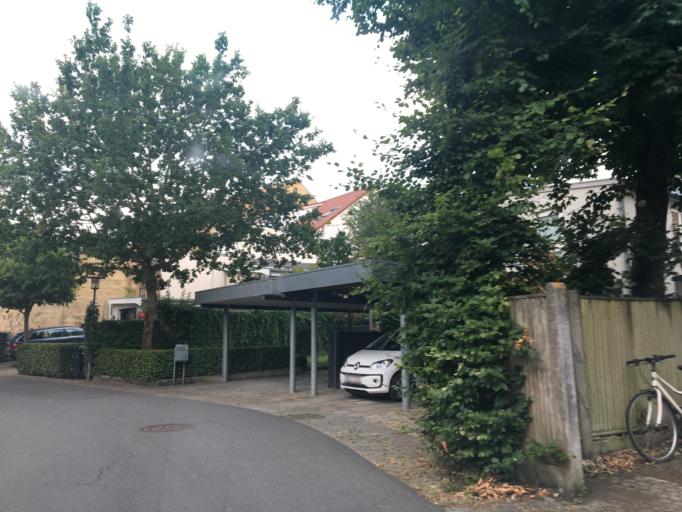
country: DK
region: Central Jutland
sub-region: Holstebro Kommune
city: Holstebro
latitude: 56.3580
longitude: 8.6215
